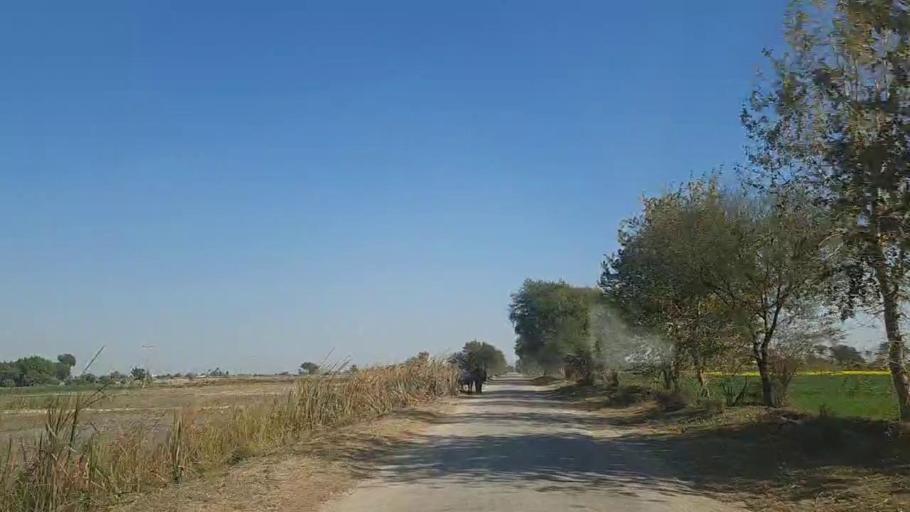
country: PK
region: Sindh
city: Sanghar
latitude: 26.2207
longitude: 68.9361
